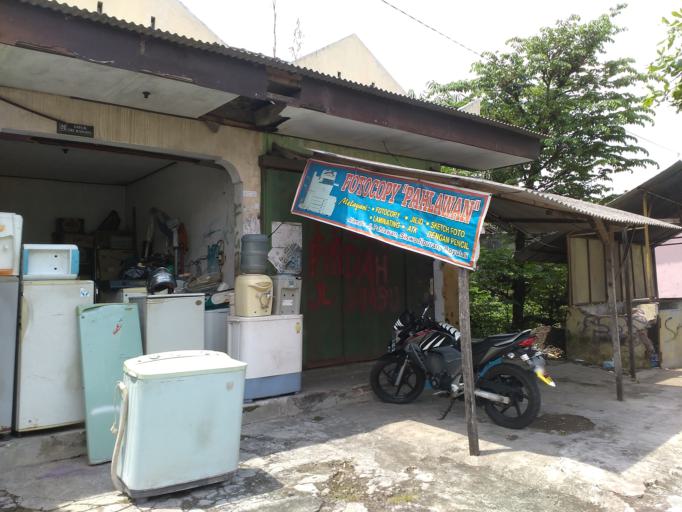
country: ID
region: Central Java
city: Boyolali
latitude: -7.5400
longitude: 110.6035
